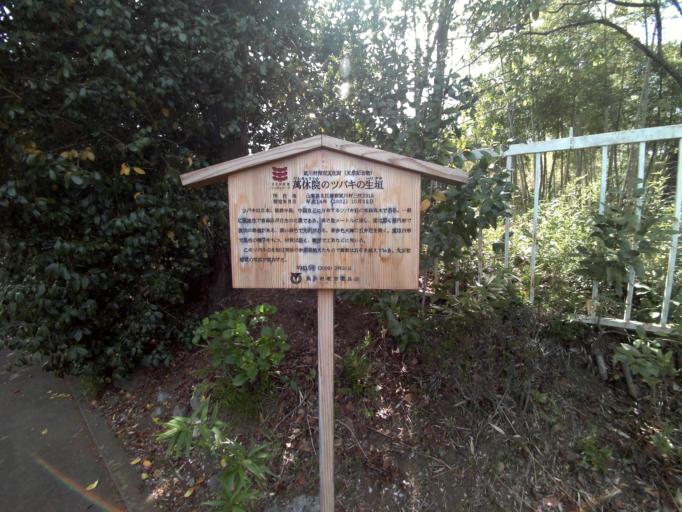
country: JP
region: Yamanashi
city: Nirasaki
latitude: 35.7903
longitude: 138.3684
